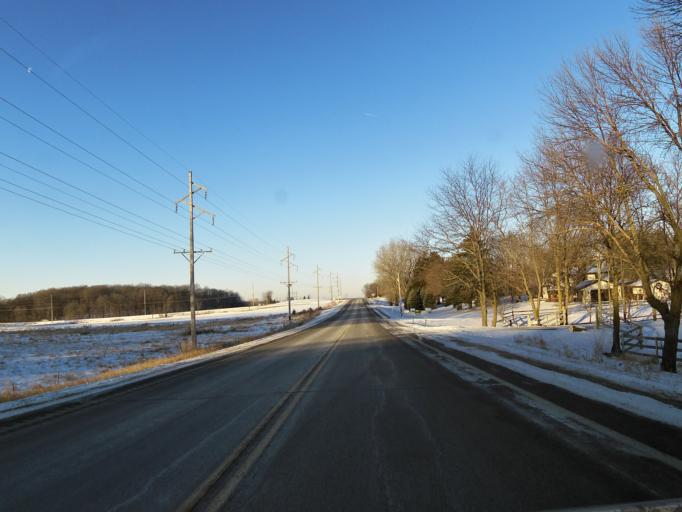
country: US
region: Minnesota
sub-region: Scott County
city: Prior Lake
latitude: 44.6741
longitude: -93.4359
